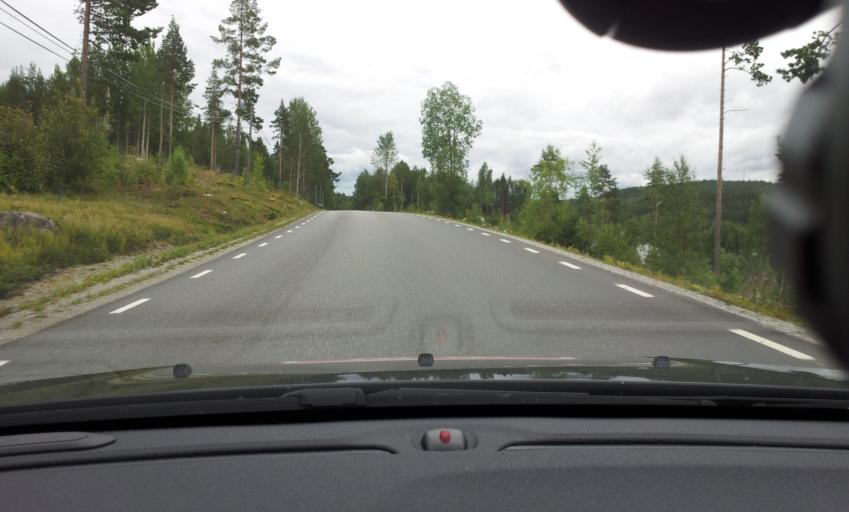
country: SE
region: Jaemtland
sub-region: Braecke Kommun
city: Braecke
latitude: 62.9682
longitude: 15.1688
